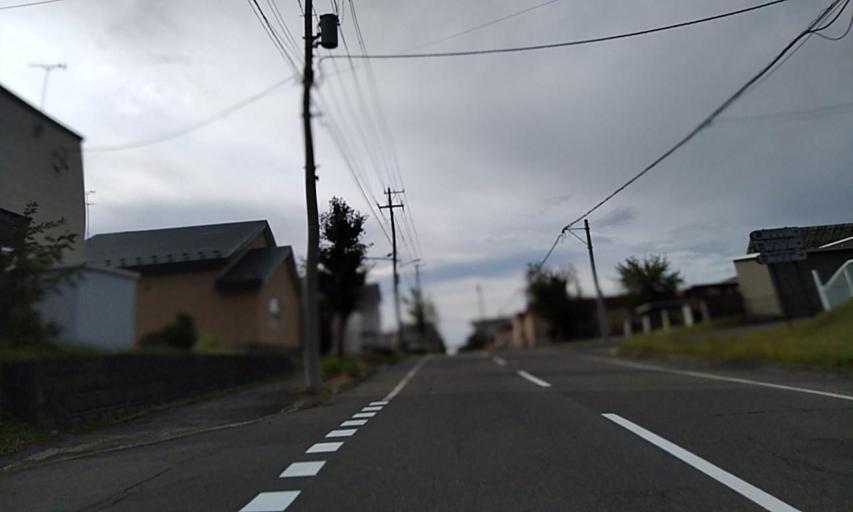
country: JP
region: Hokkaido
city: Obihiro
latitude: 42.9140
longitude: 143.0426
